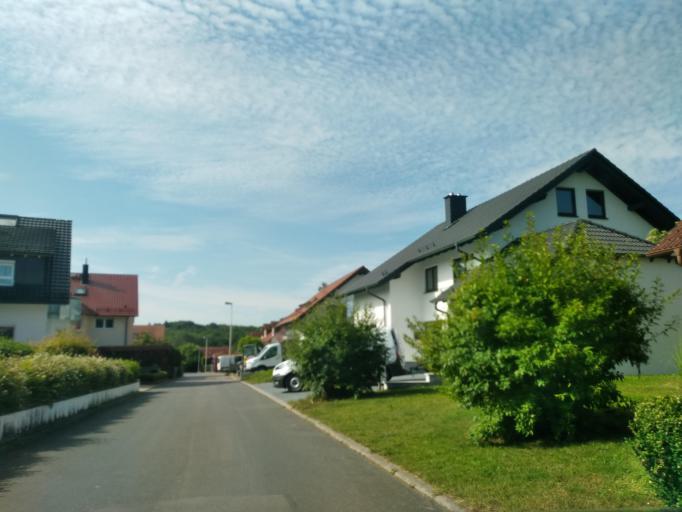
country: DE
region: Baden-Wuerttemberg
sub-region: Karlsruhe Region
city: Buchen
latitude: 49.5183
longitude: 9.3003
